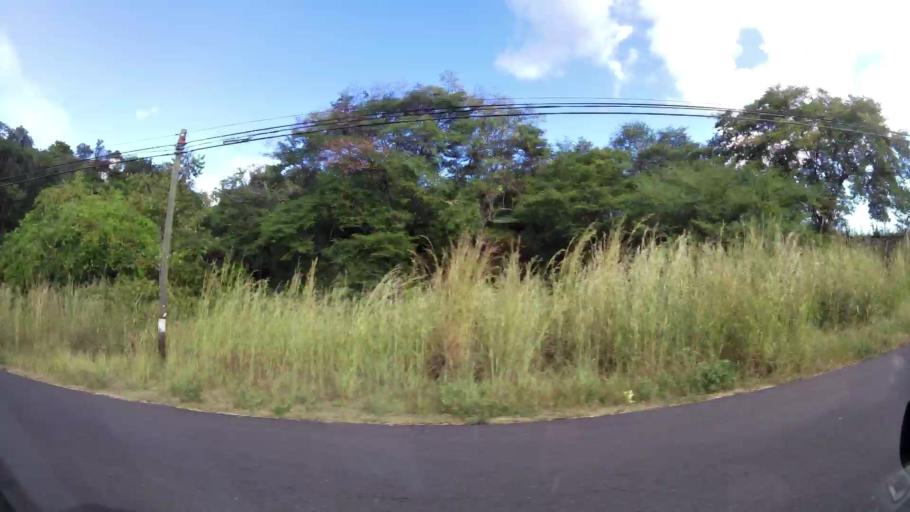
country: CR
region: Guanacaste
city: Sardinal
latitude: 10.5619
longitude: -85.6794
